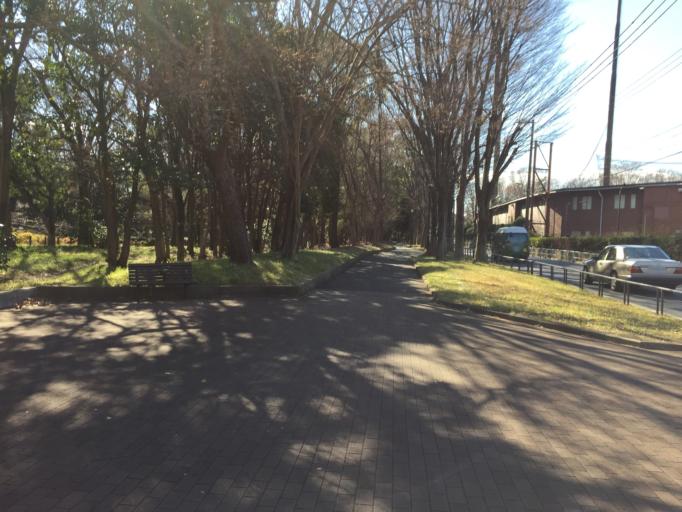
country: JP
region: Tokyo
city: Chofugaoka
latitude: 35.6313
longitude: 139.6154
